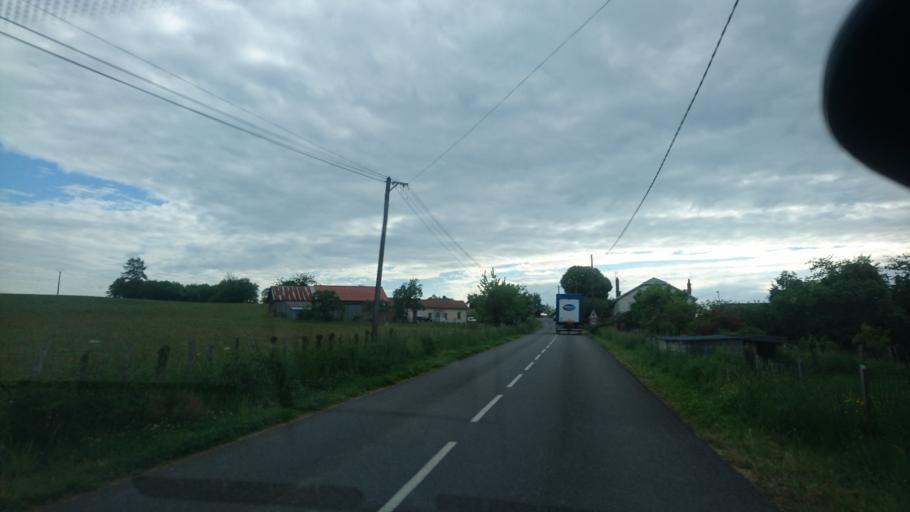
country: FR
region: Limousin
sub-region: Departement de la Haute-Vienne
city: Chateauneuf-la-Foret
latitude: 45.6827
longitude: 1.5820
